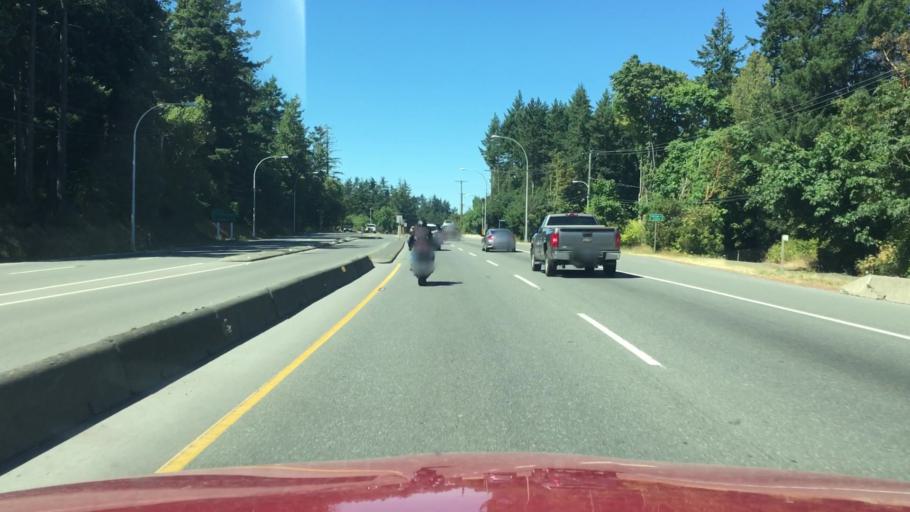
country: CA
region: British Columbia
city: Victoria
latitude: 48.5433
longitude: -123.3902
